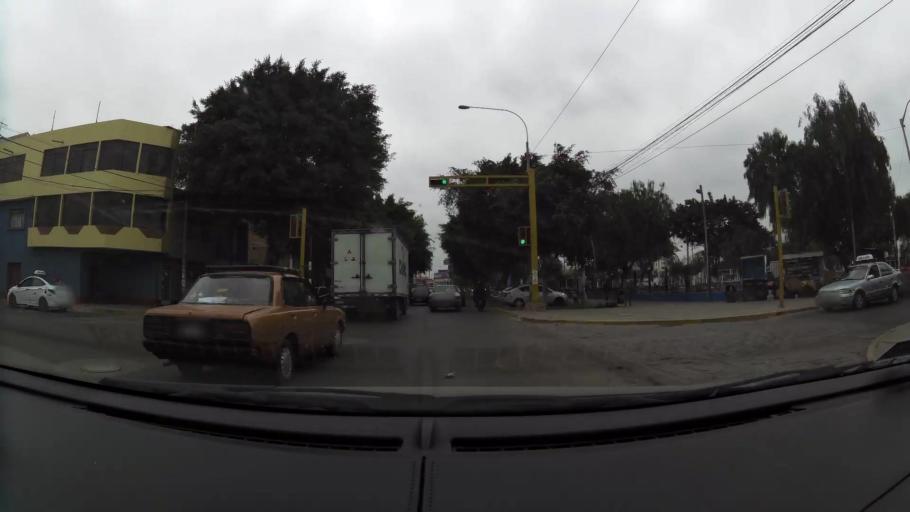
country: PE
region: La Libertad
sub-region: Provincia de Trujillo
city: Trujillo
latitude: -8.1072
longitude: -79.0320
